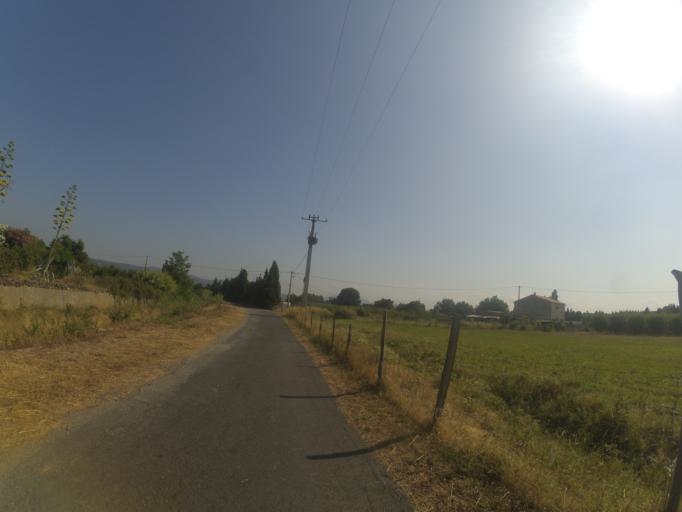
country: FR
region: Languedoc-Roussillon
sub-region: Departement des Pyrenees-Orientales
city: Ille-sur-Tet
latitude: 42.6580
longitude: 2.6248
